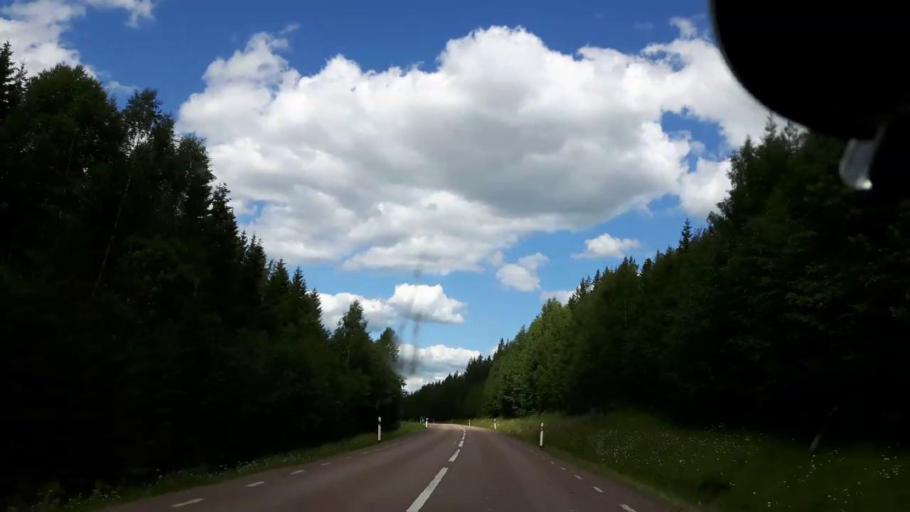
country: SE
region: Jaemtland
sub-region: Ragunda Kommun
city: Hammarstrand
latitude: 62.9211
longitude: 16.7037
